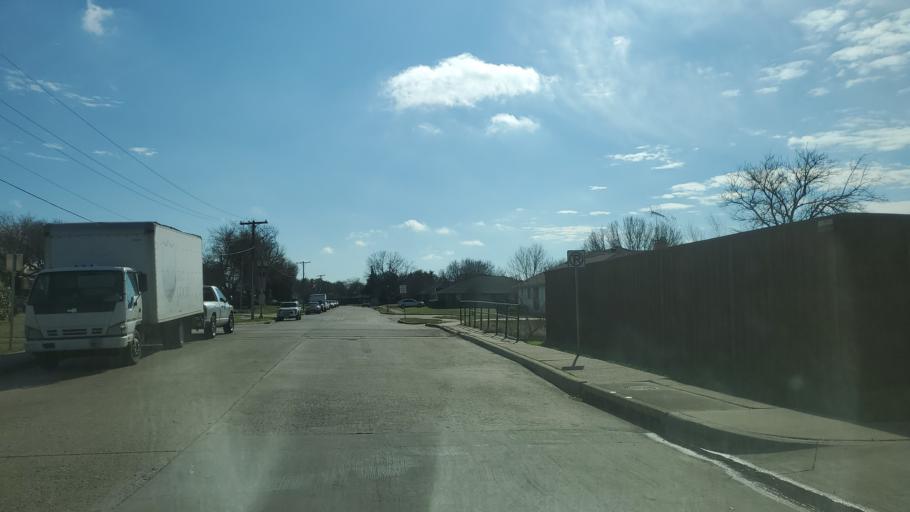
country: US
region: Texas
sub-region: Dallas County
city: Carrollton
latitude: 32.9844
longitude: -96.8801
